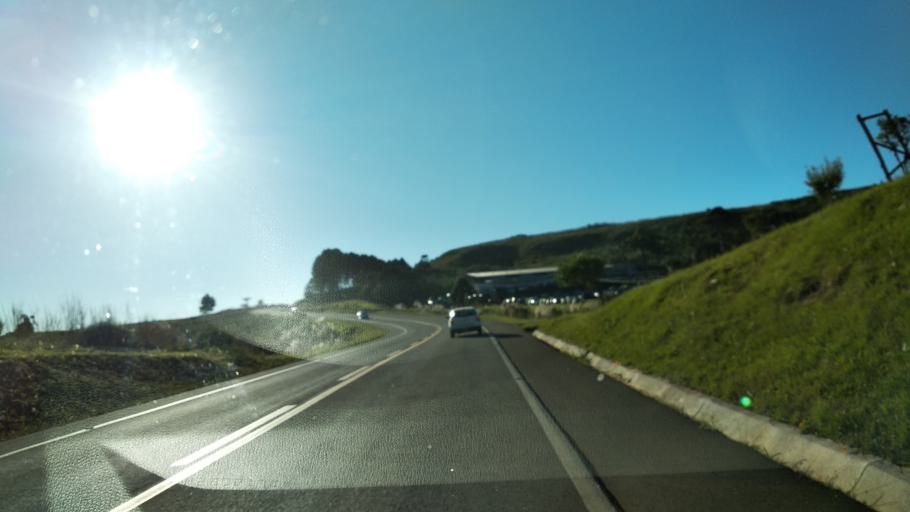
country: BR
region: Santa Catarina
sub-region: Lages
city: Lages
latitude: -27.7882
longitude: -50.4298
